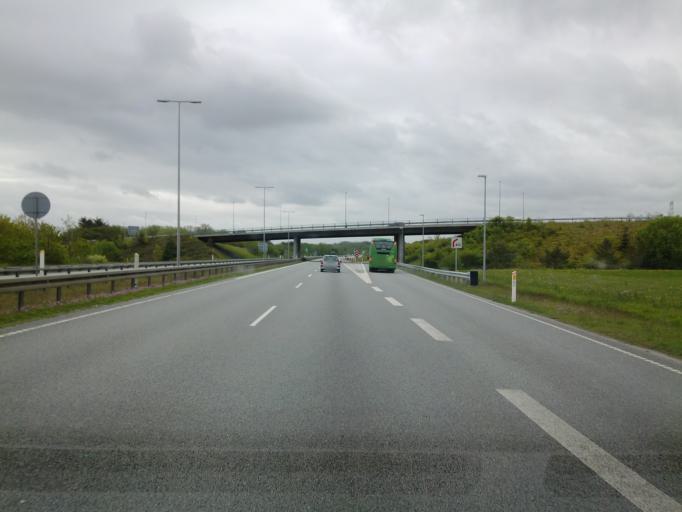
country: DK
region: North Denmark
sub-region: Frederikshavn Kommune
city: Saeby
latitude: 57.3826
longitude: 10.5079
